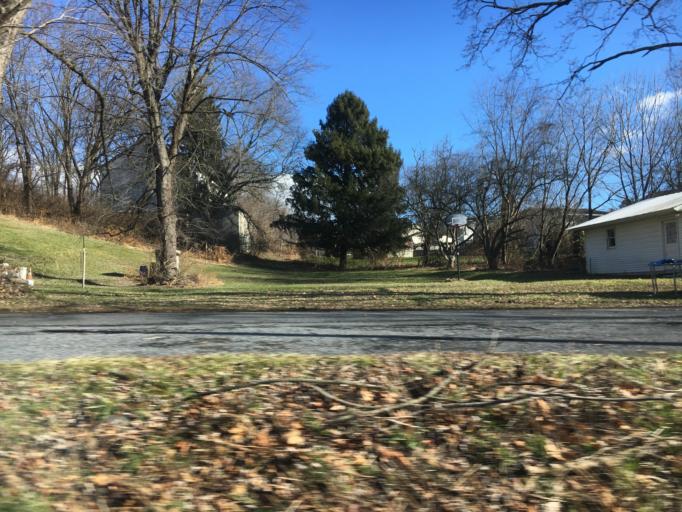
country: US
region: Pennsylvania
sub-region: Lehigh County
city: Stiles
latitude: 40.6359
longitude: -75.5087
